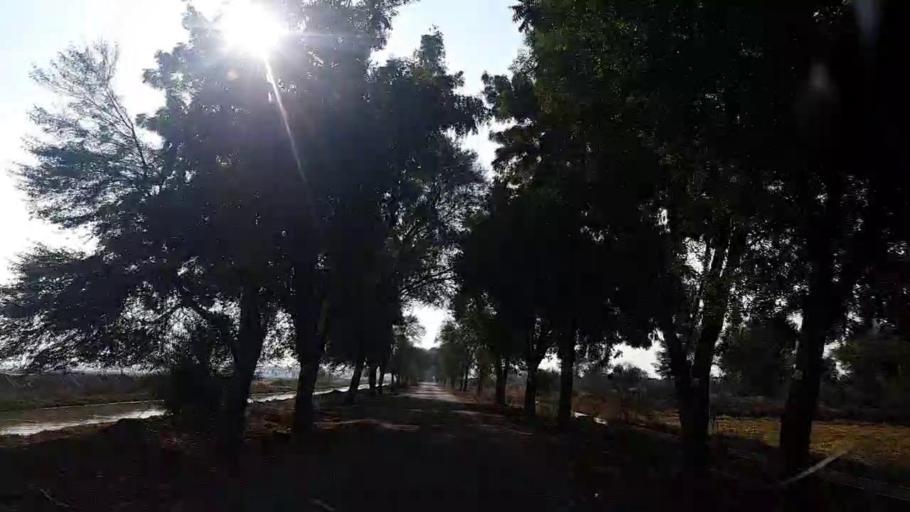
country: PK
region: Sindh
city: Khanpur
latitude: 27.6409
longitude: 69.5991
